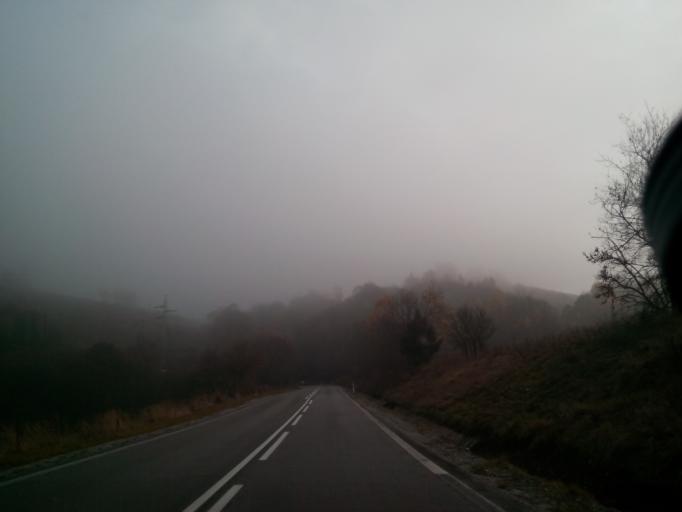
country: SK
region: Kosicky
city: Gelnica
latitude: 48.8508
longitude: 21.0257
